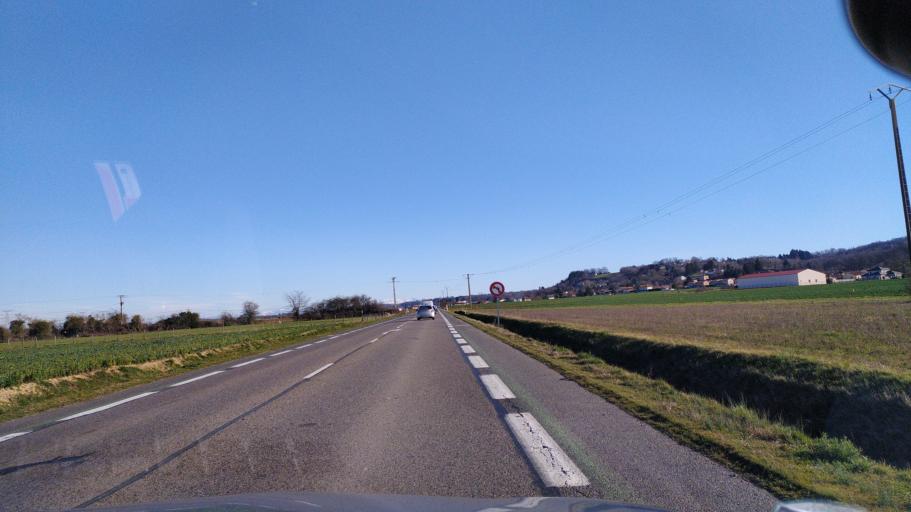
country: FR
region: Rhone-Alpes
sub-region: Departement du Rhone
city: Saint-Pierre-de-Chandieu
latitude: 45.6537
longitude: 5.0141
